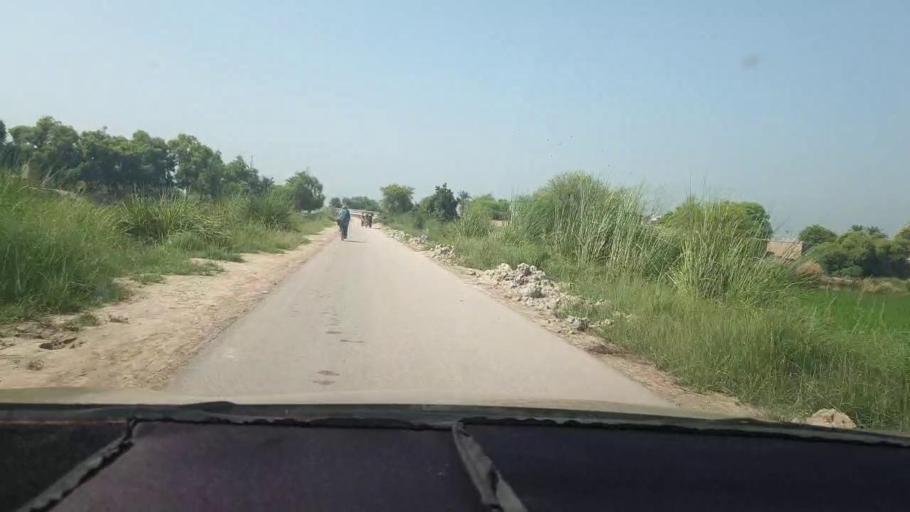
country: PK
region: Sindh
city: Kambar
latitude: 27.5787
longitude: 68.0449
